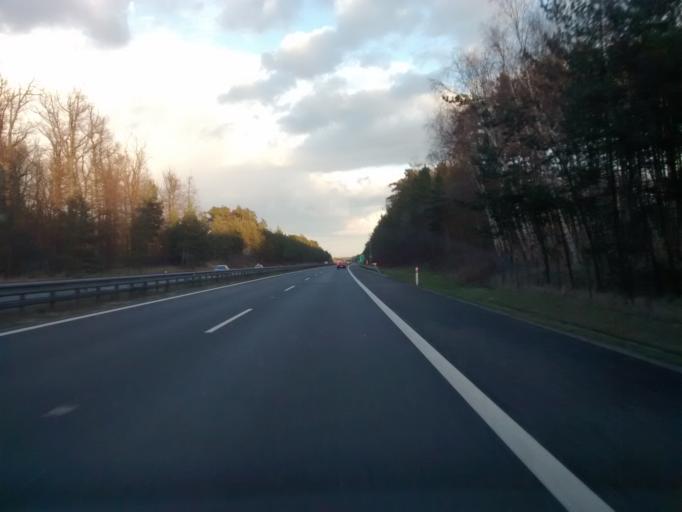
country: CZ
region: Central Bohemia
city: Poricany
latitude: 50.1236
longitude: 14.9270
